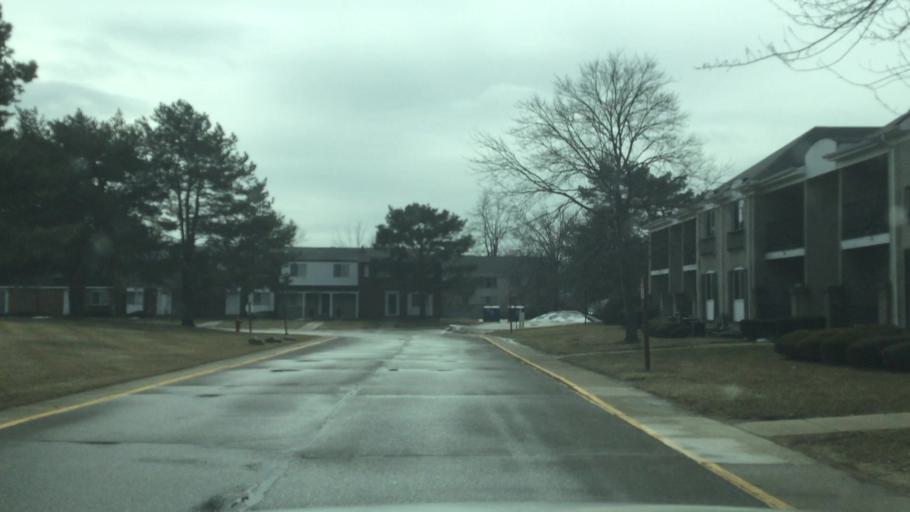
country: US
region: Michigan
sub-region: Oakland County
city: Southfield
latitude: 42.4639
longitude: -83.2083
